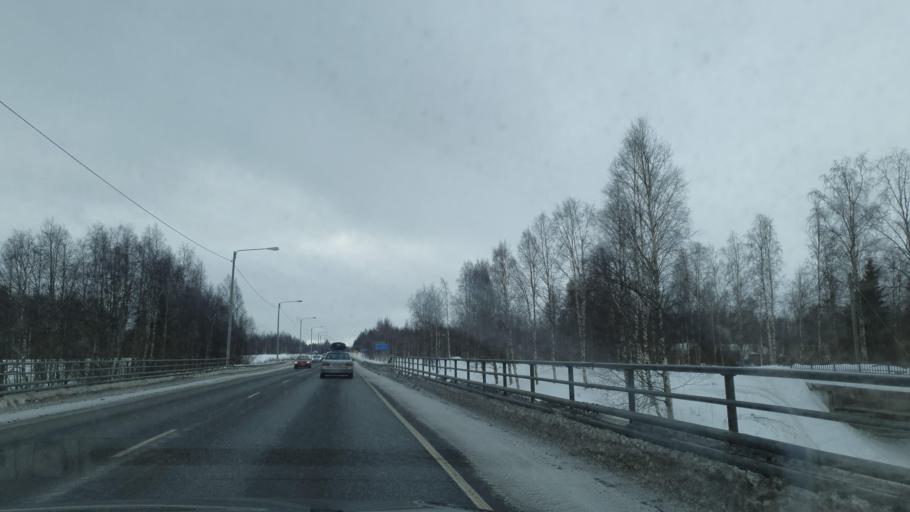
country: FI
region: Lapland
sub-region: Kemi-Tornio
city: Tornio
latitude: 65.8686
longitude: 24.1677
